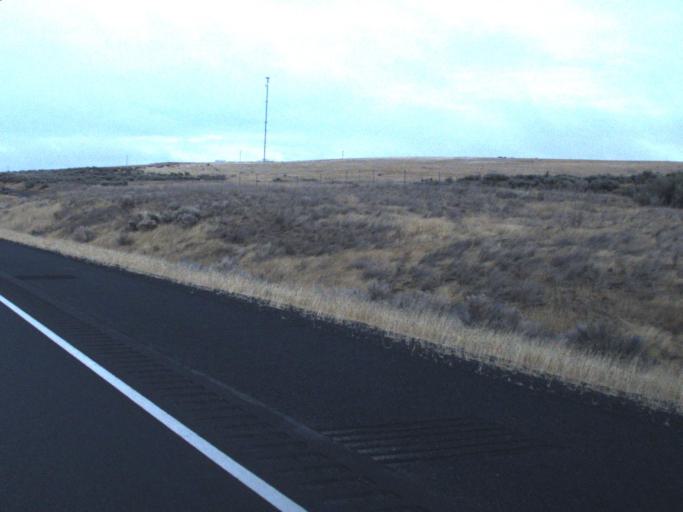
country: US
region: Washington
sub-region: Grant County
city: Warden
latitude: 47.0877
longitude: -118.9282
